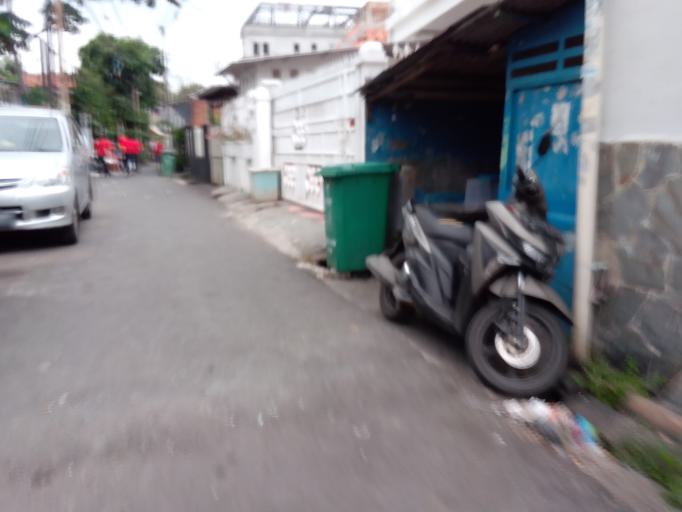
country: ID
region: Jakarta Raya
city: Jakarta
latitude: -6.1741
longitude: 106.8143
